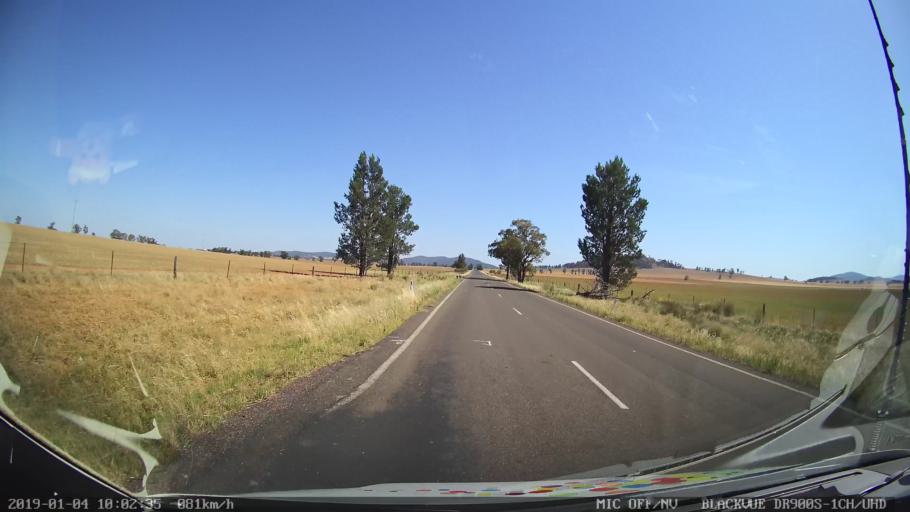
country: AU
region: New South Wales
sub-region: Cabonne
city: Canowindra
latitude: -33.4745
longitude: 148.3653
